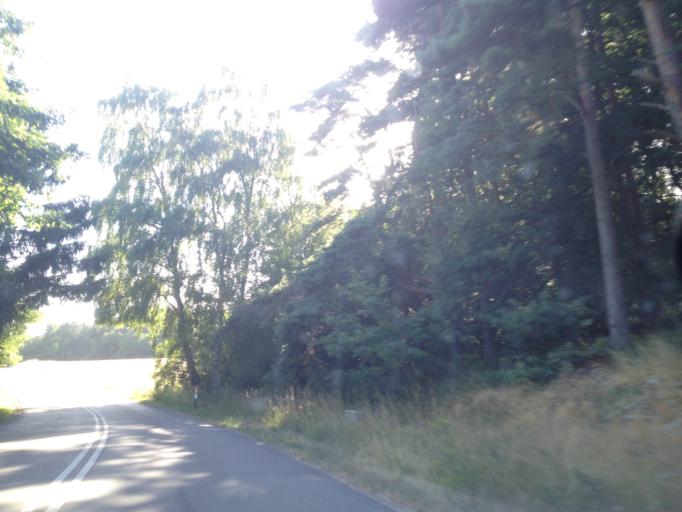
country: DK
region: Capital Region
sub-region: Halsnaes Kommune
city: Frederiksvaerk
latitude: 56.0296
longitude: 12.0873
